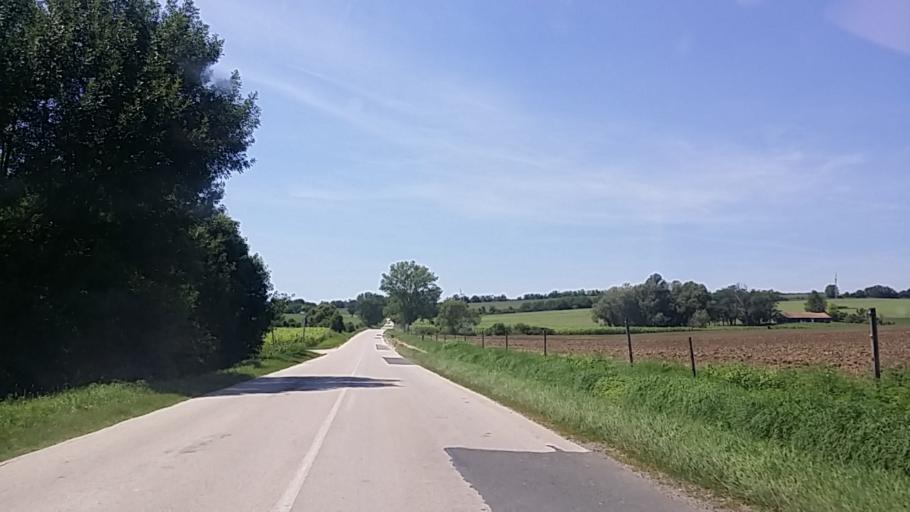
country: HU
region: Somogy
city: Tab
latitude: 46.7398
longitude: 18.0713
